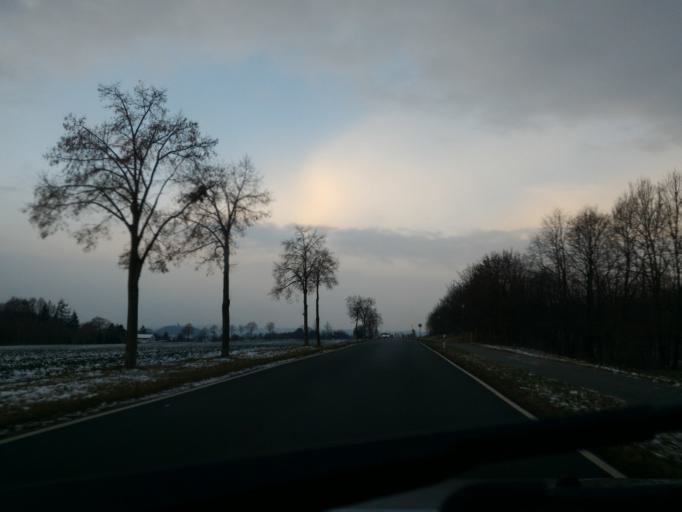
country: DE
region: Saxony
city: Leutersdorf
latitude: 50.9481
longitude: 14.6310
